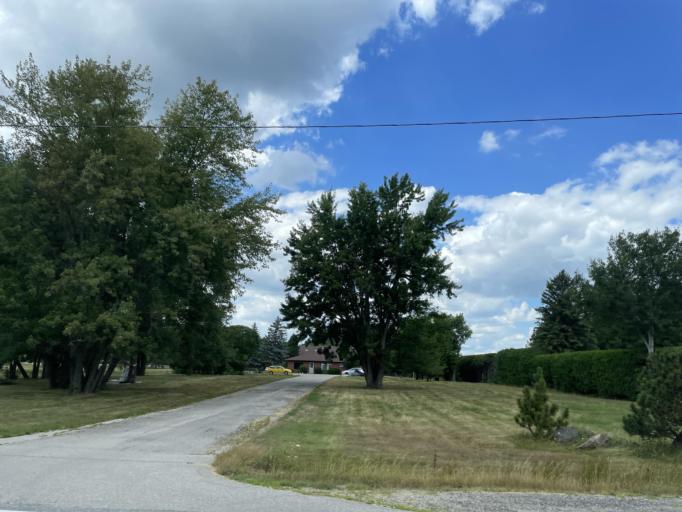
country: CA
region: Ontario
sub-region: Wellington County
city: Guelph
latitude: 43.5573
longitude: -80.3386
